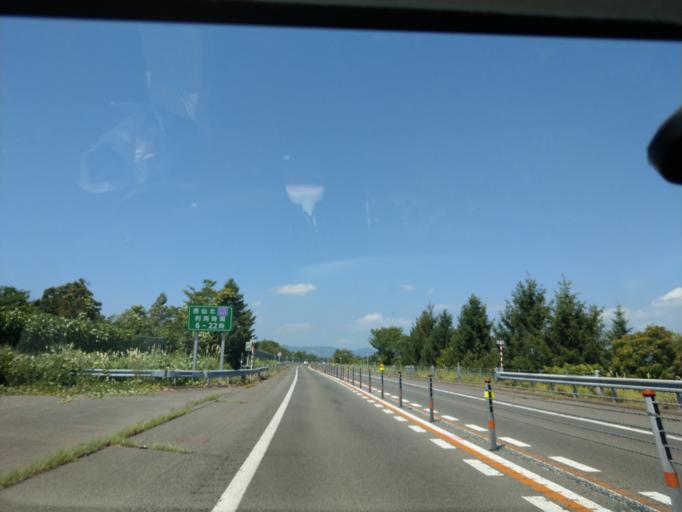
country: JP
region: Akita
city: Yokotemachi
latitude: 39.3447
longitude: 140.4997
